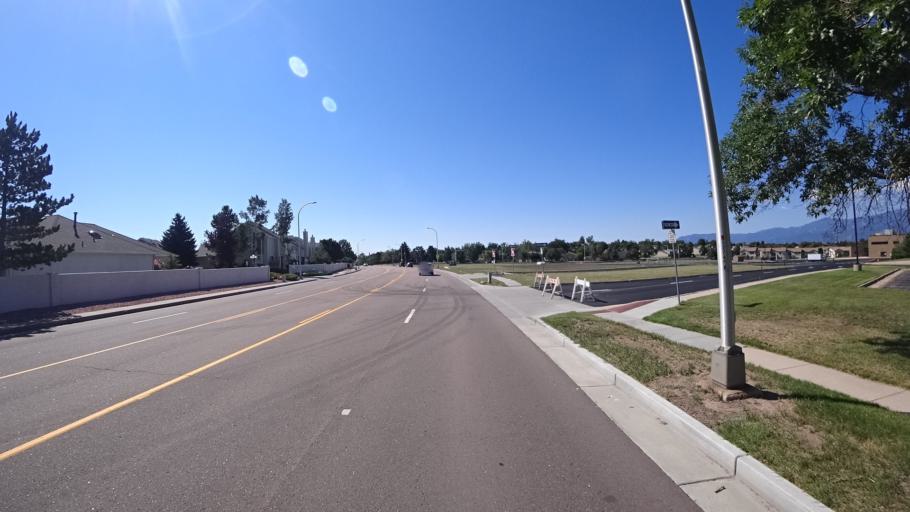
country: US
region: Colorado
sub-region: El Paso County
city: Black Forest
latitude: 38.9500
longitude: -104.7707
